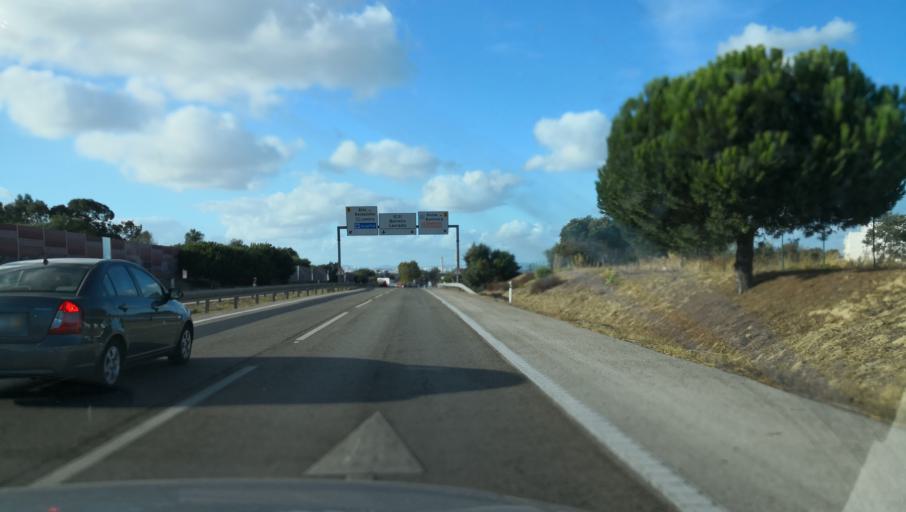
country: PT
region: Setubal
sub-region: Barreiro
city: Barreiro
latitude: 38.6536
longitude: -9.0538
